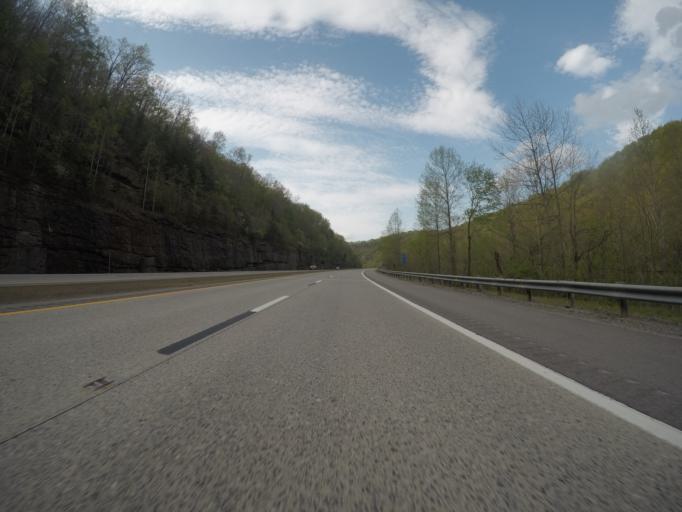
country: US
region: West Virginia
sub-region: Kanawha County
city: Alum Creek
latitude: 38.1916
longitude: -81.8464
